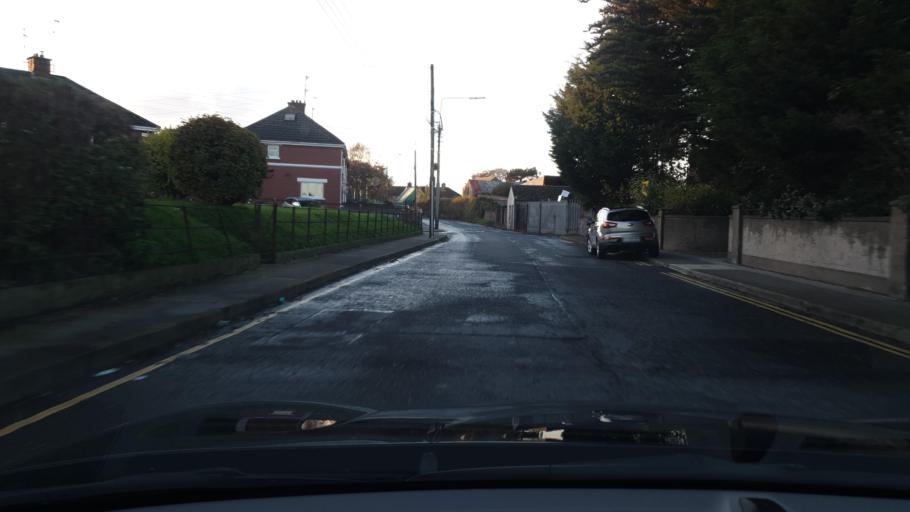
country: IE
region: Leinster
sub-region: Lu
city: Drogheda
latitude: 53.7219
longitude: -6.3463
